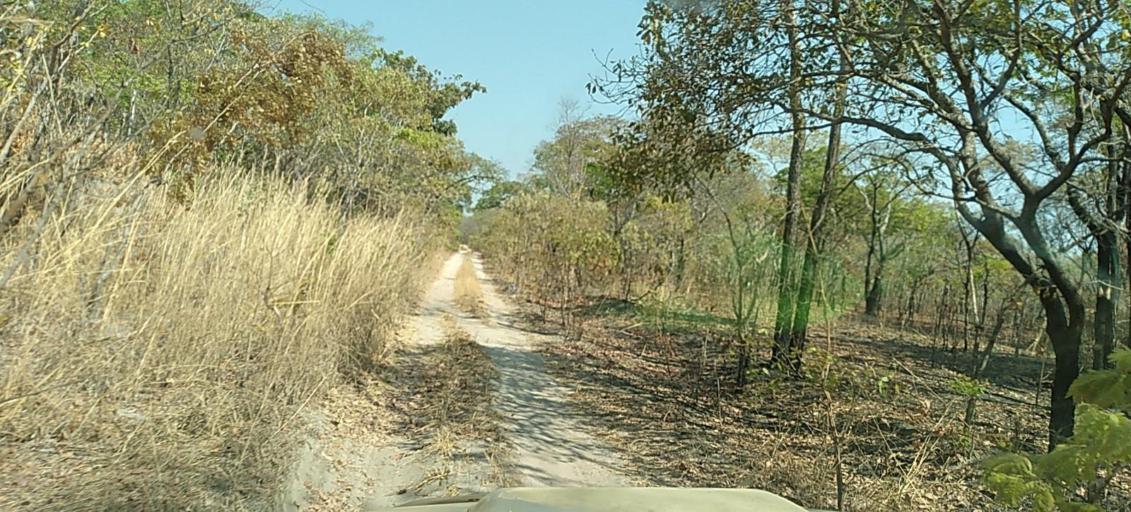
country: ZM
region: North-Western
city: Kalengwa
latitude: -13.3287
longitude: 24.8361
